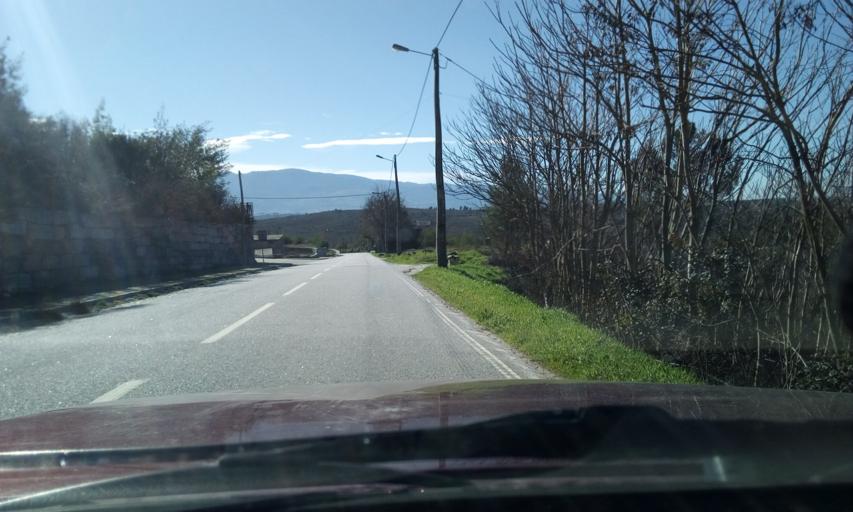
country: PT
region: Guarda
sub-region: Fornos de Algodres
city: Fornos de Algodres
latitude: 40.6117
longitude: -7.5336
